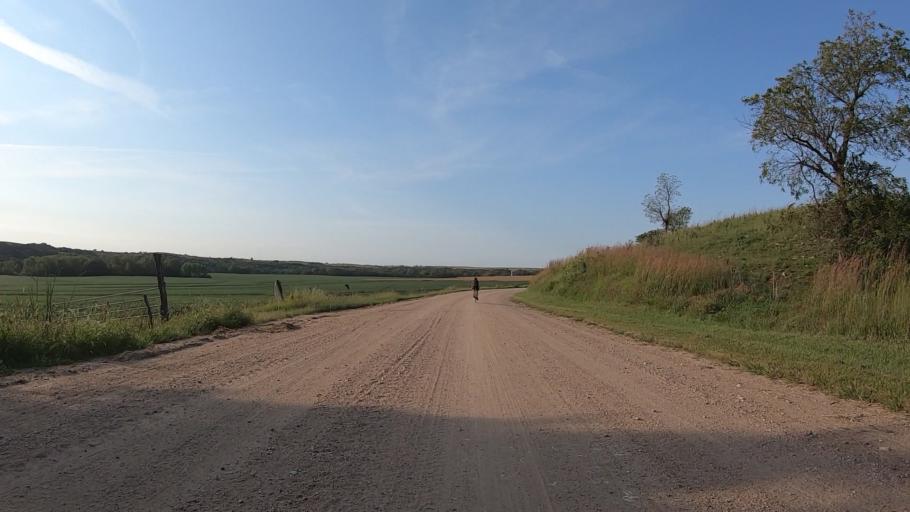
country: US
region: Kansas
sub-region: Marshall County
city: Blue Rapids
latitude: 39.6824
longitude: -96.7792
